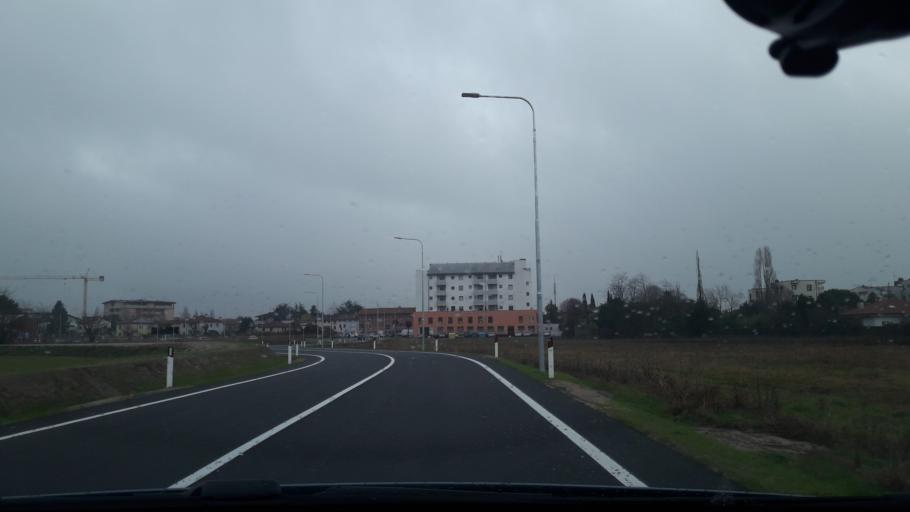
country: IT
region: Friuli Venezia Giulia
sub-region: Provincia di Udine
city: Basaldella
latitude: 46.0499
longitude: 13.2204
